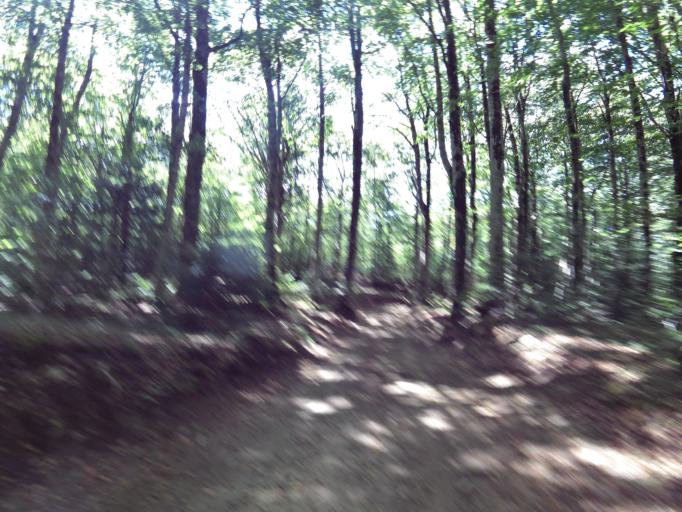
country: IT
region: Calabria
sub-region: Provincia di Vibo-Valentia
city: Mongiana
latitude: 38.5244
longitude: 16.3459
